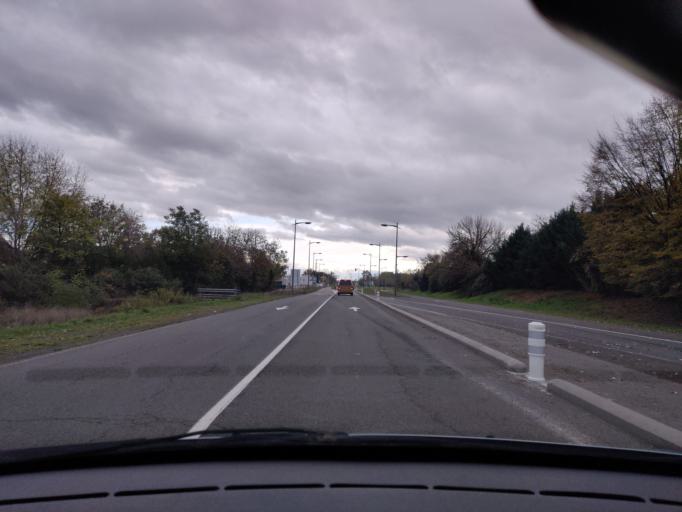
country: FR
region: Auvergne
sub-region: Departement du Puy-de-Dome
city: Menetrol
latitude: 45.8811
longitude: 3.1133
